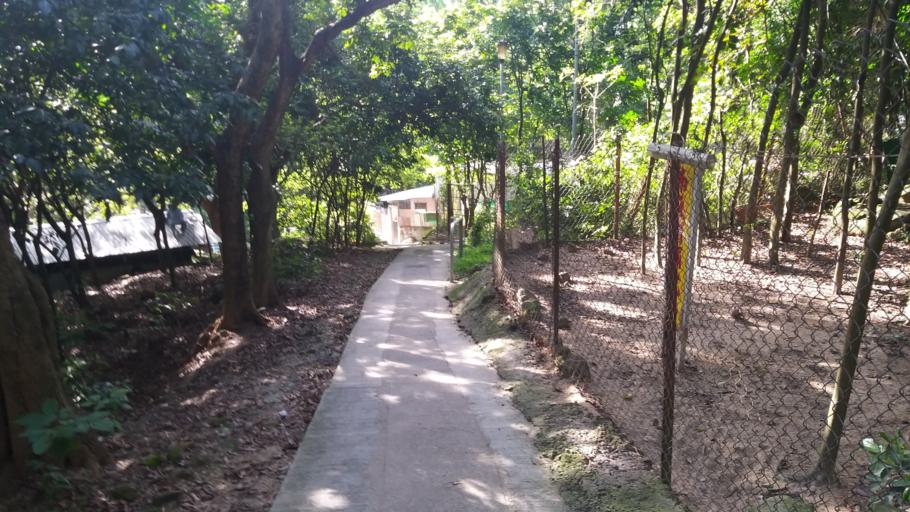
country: HK
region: Tuen Mun
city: Tuen Mun
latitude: 22.3953
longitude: 113.9795
